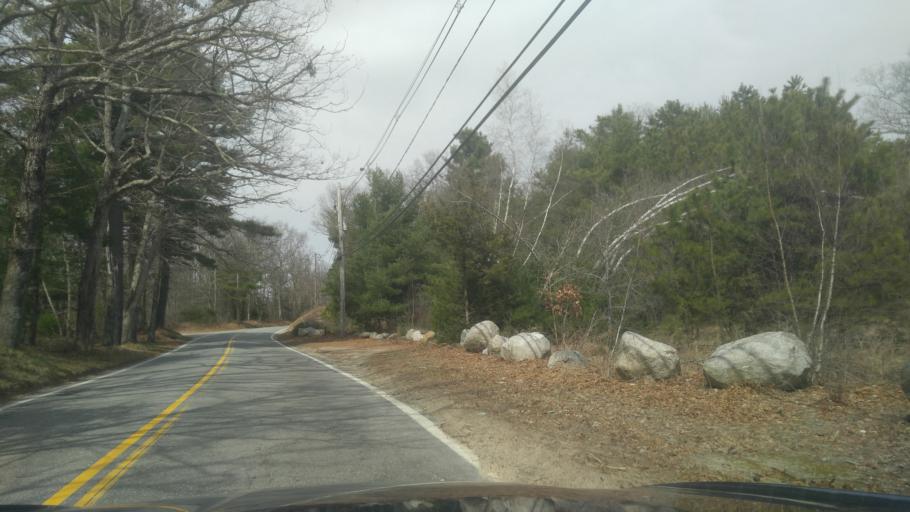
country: US
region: Rhode Island
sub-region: Kent County
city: West Warwick
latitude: 41.6449
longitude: -71.5736
